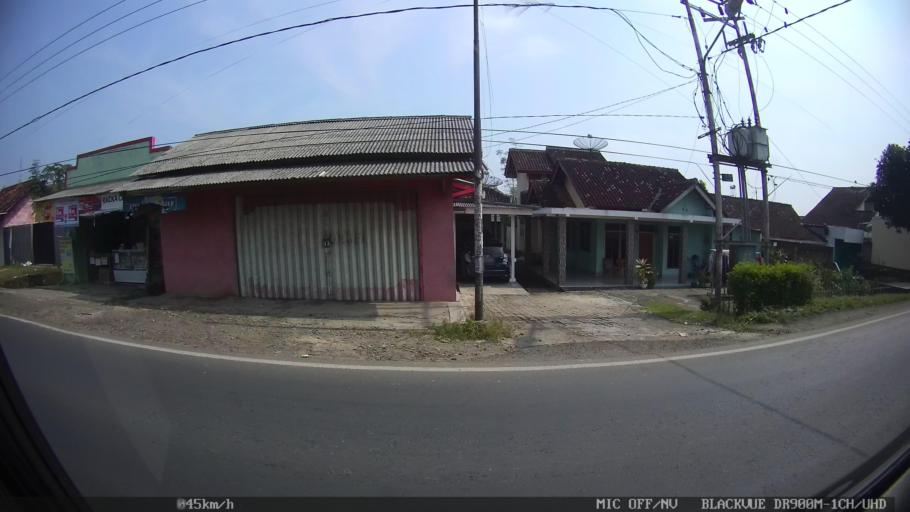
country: ID
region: Lampung
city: Gedongtataan
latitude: -5.3758
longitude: 105.0907
